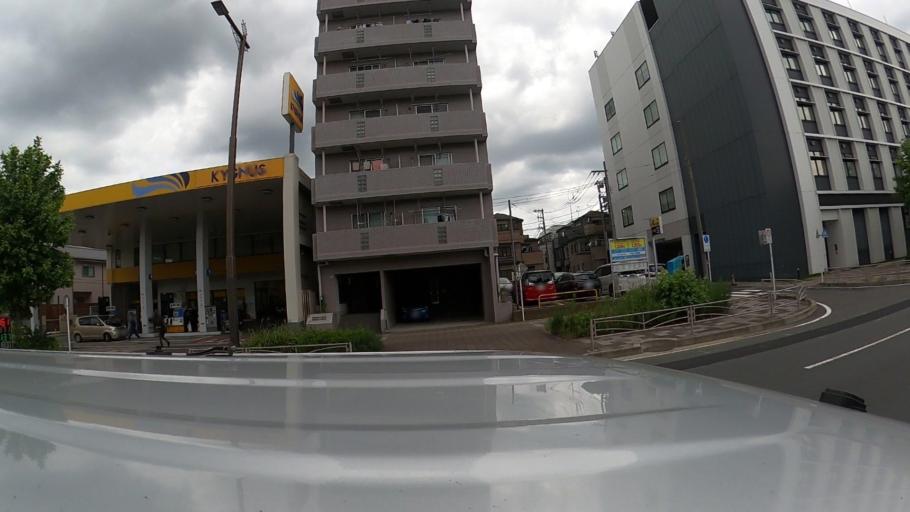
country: JP
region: Kanagawa
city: Yokohama
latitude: 35.4798
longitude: 139.6395
